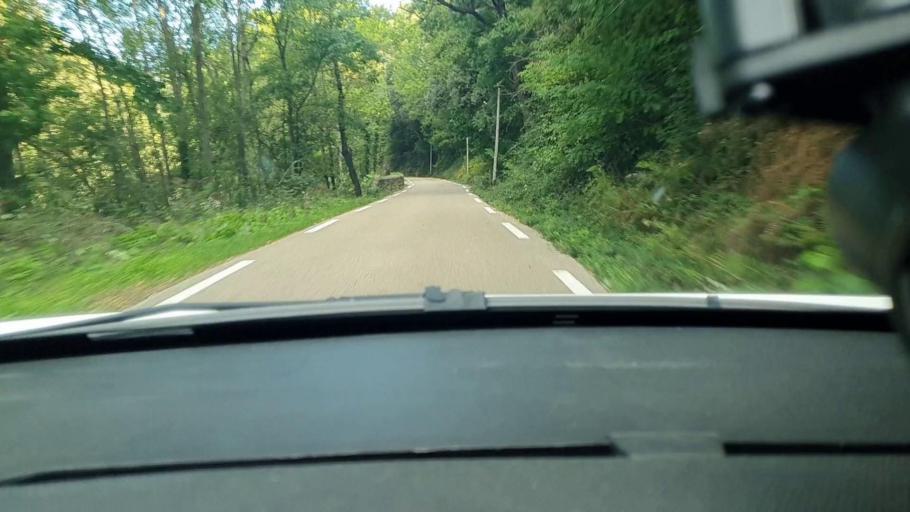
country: FR
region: Languedoc-Roussillon
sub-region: Departement du Gard
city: Besseges
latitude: 44.3807
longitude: 3.9855
